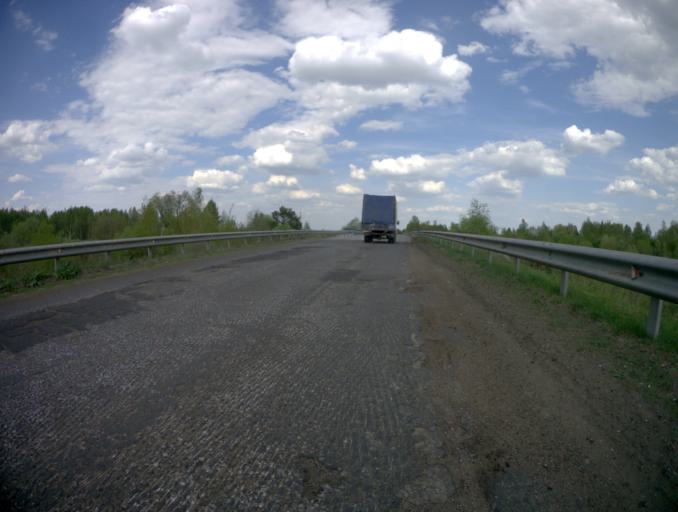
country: RU
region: Vladimir
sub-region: Kovrovskiy Rayon
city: Kovrov
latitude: 56.4331
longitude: 41.2523
